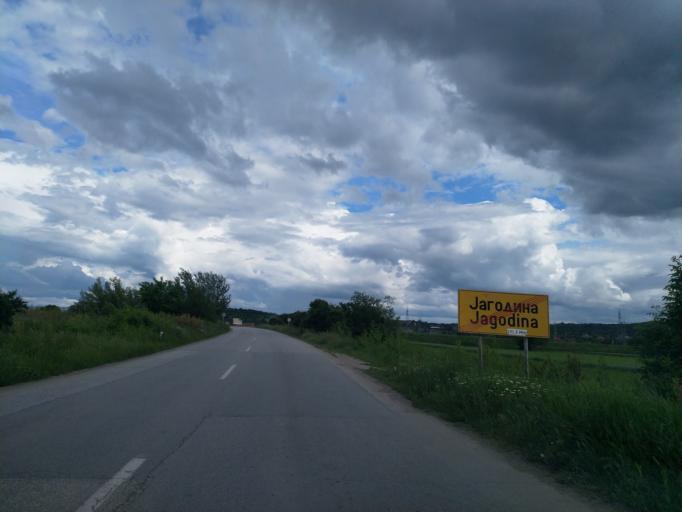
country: RS
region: Central Serbia
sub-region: Pomoravski Okrug
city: Jagodina
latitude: 43.9591
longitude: 21.2866
